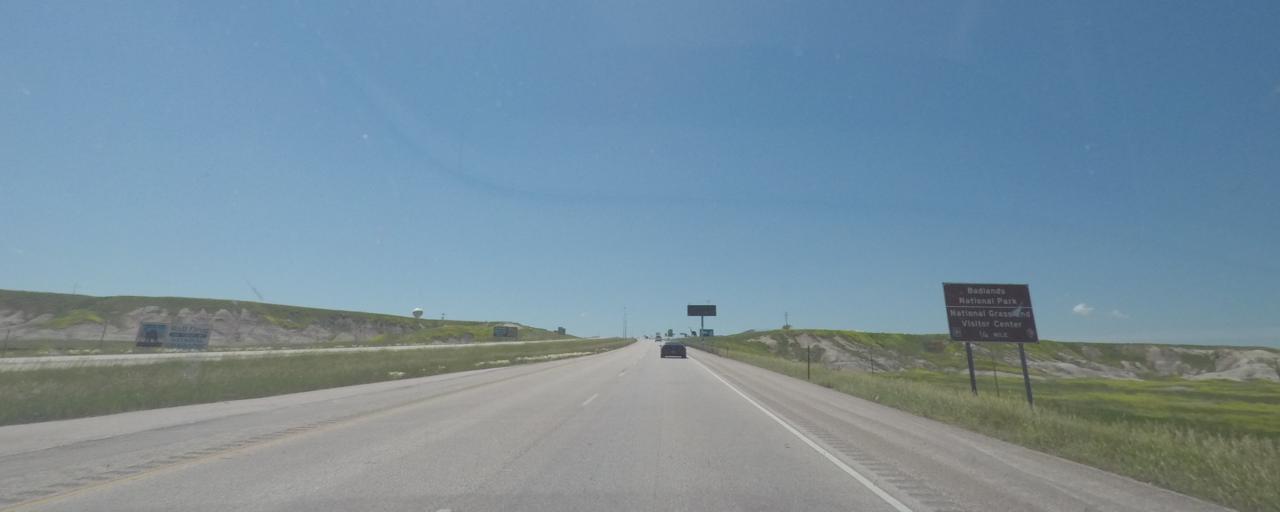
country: US
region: South Dakota
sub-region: Haakon County
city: Philip
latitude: 43.9877
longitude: -102.2256
